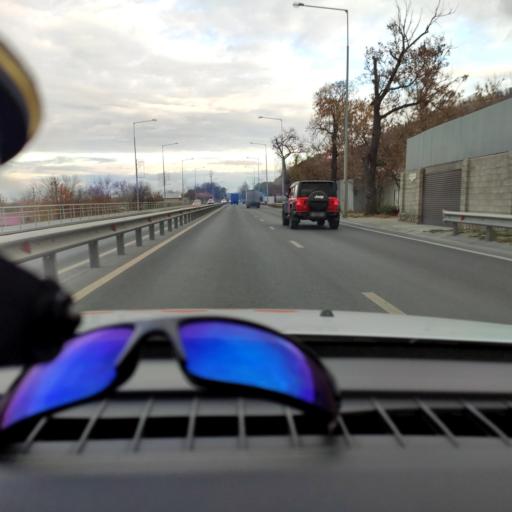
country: RU
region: Samara
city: Volzhskiy
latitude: 53.3986
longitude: 50.1502
